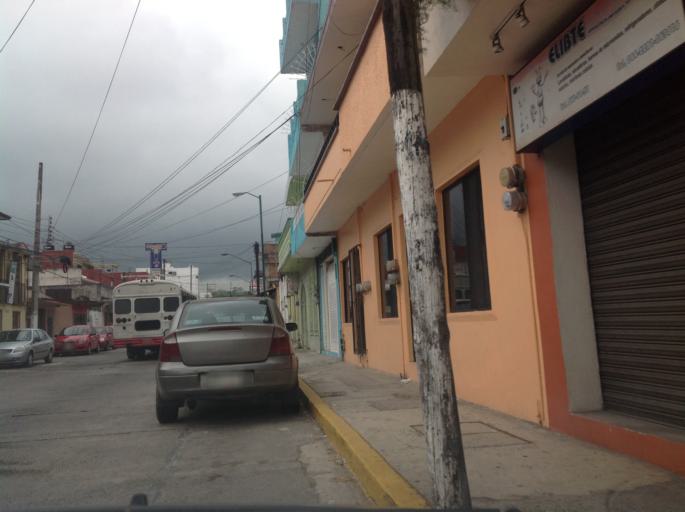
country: MX
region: Veracruz
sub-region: Xalapa
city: Xalapa de Enriquez
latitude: 19.5208
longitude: -96.9237
